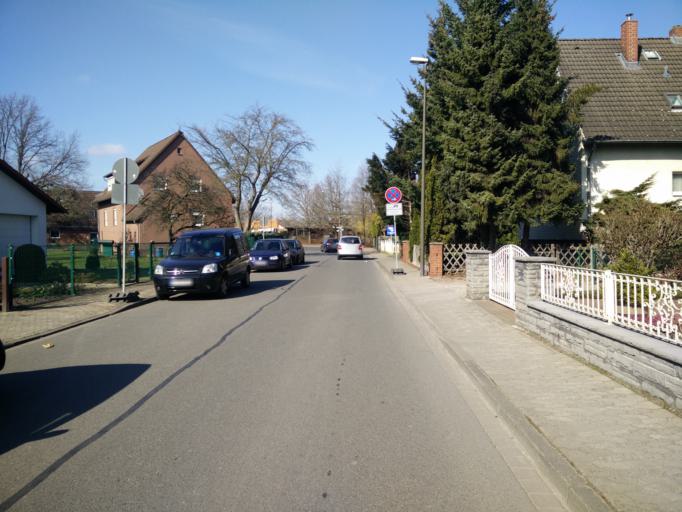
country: DE
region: Lower Saxony
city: Langenhagen
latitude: 52.4311
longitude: 9.7225
